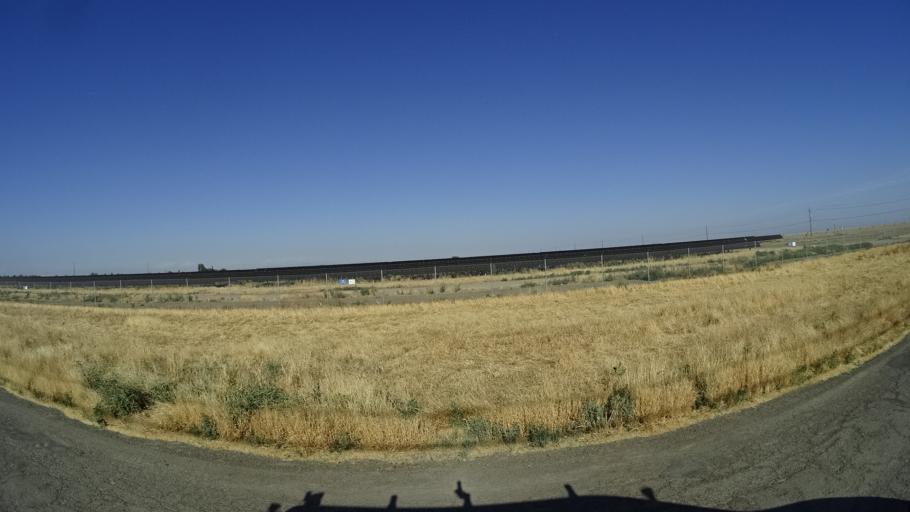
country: US
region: California
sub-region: Kings County
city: Corcoran
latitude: 36.1363
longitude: -119.5541
